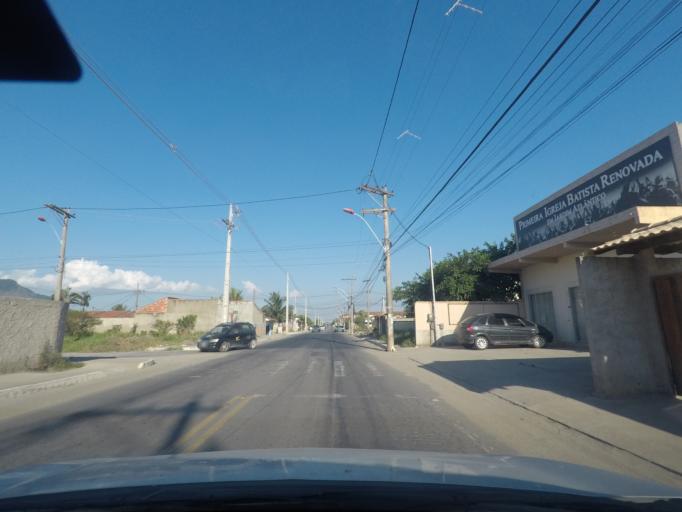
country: BR
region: Rio de Janeiro
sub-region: Marica
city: Marica
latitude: -22.9567
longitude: -42.9458
